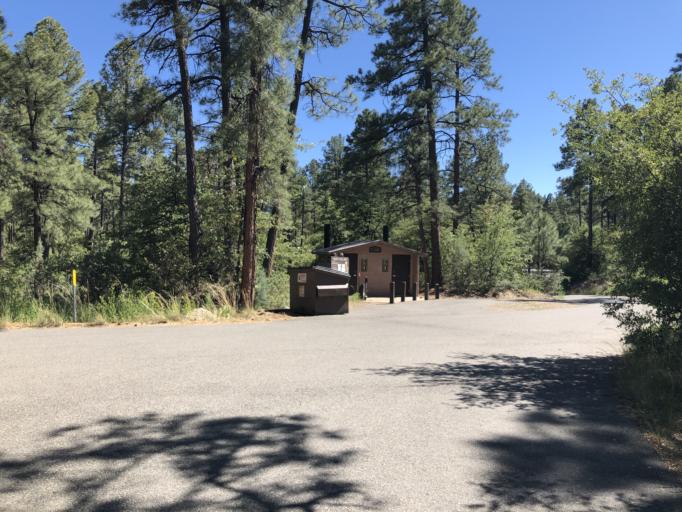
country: US
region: Arizona
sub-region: Yavapai County
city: Prescott
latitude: 34.5193
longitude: -112.3902
